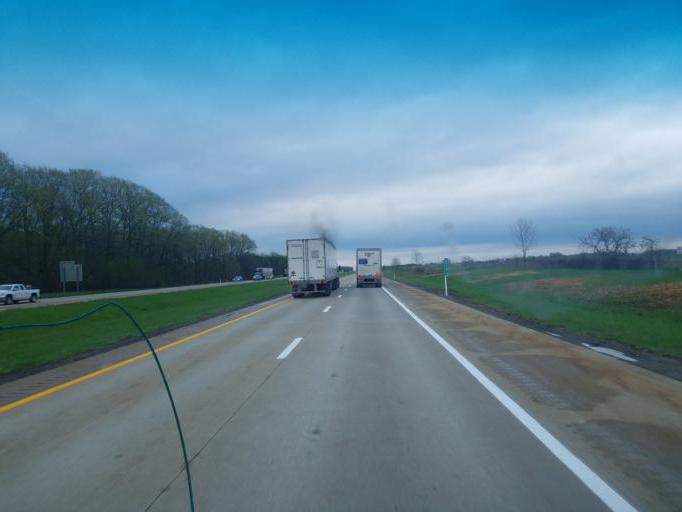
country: US
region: Ohio
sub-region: Ashtabula County
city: Geneva
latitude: 41.7698
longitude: -80.9267
